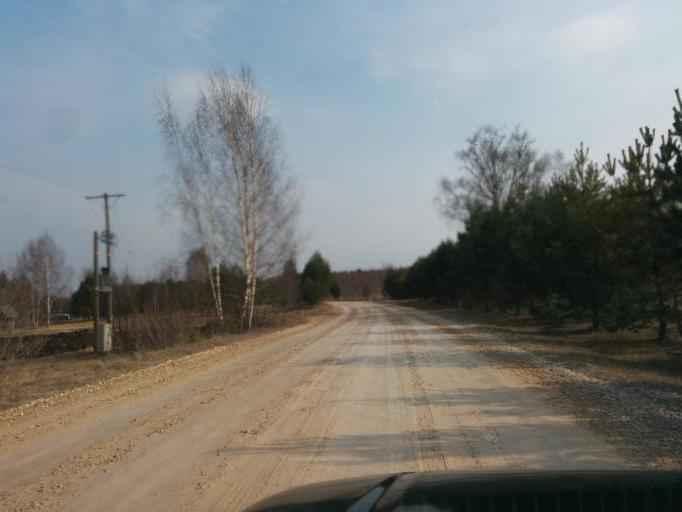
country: LV
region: Olaine
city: Olaine
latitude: 56.7916
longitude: 23.9940
